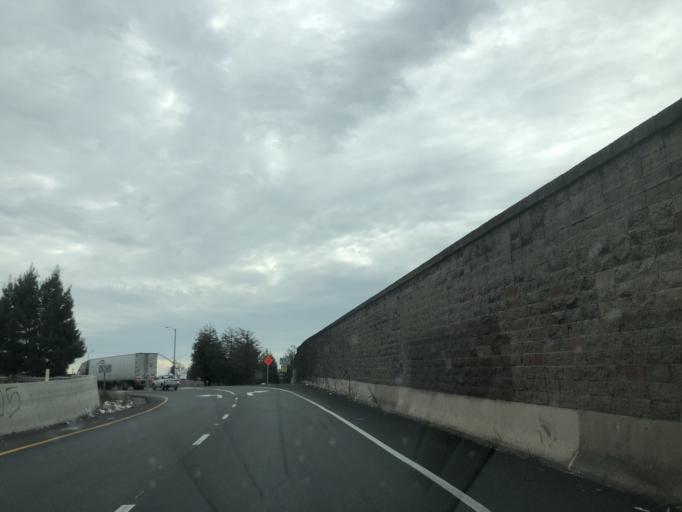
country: US
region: California
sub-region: Alameda County
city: San Leandro
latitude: 37.7322
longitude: -122.1902
